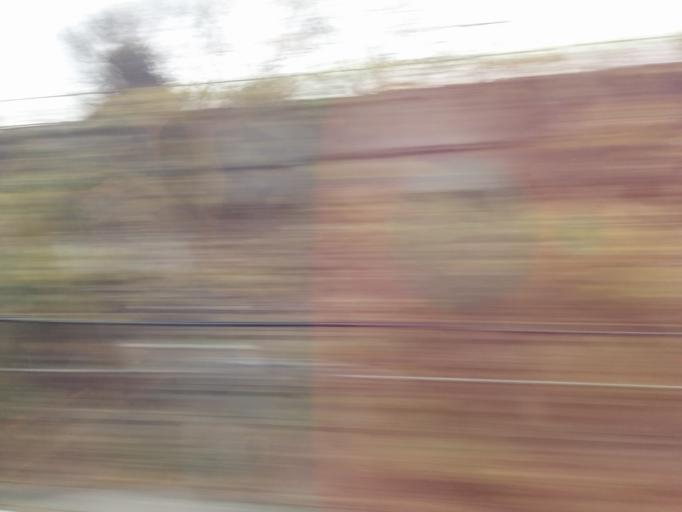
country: JP
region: Kanagawa
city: Minami-rinkan
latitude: 35.4405
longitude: 139.4882
